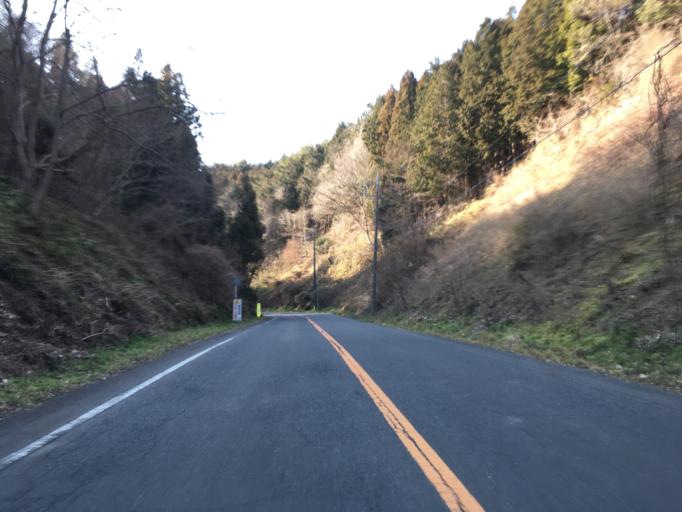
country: JP
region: Ibaraki
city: Daigo
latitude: 36.7354
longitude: 140.5225
